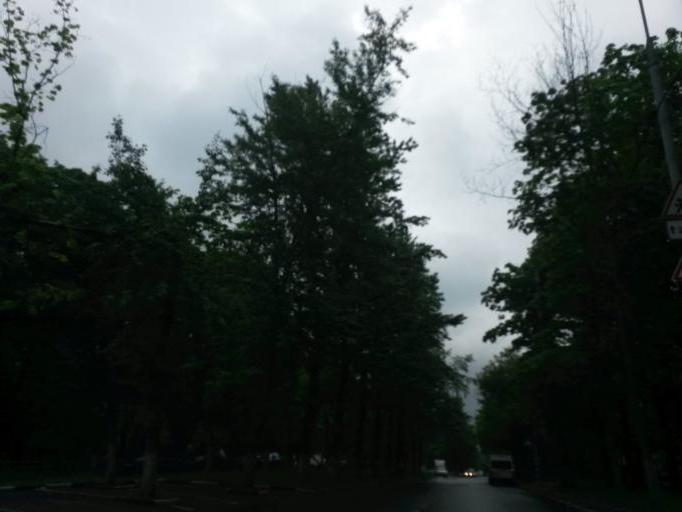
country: RU
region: Moscow
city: Novyye Cheremushki
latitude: 55.6928
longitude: 37.5847
